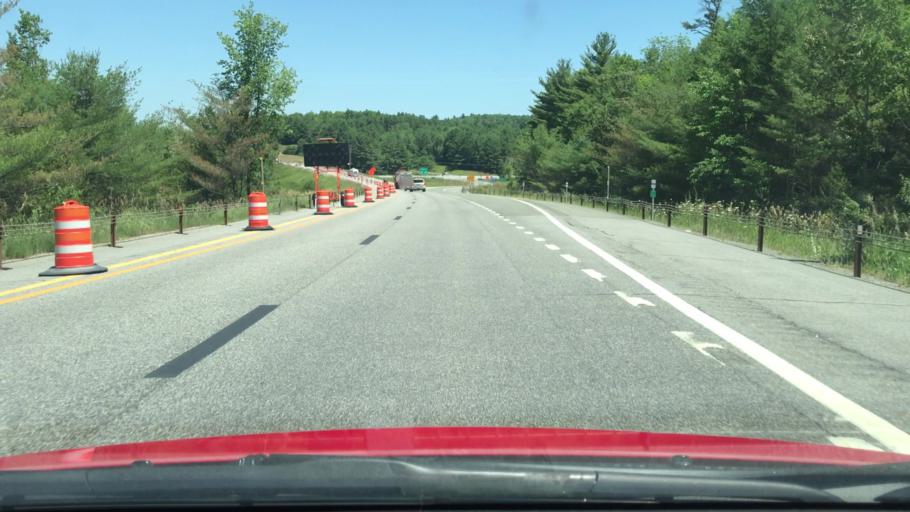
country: US
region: New York
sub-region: Essex County
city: Elizabethtown
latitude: 44.2051
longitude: -73.5086
